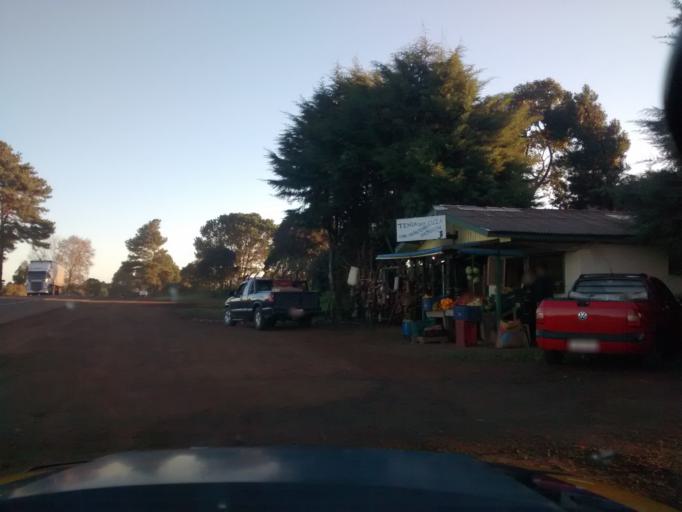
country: BR
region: Rio Grande do Sul
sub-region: Vacaria
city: Vacaria
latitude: -28.5442
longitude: -50.9735
